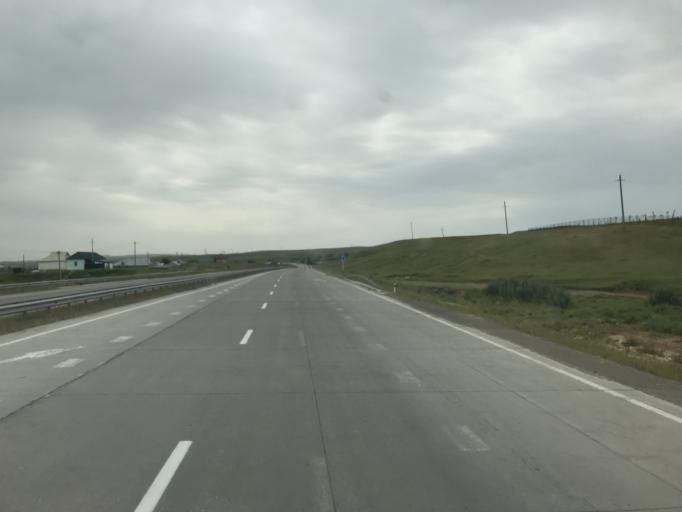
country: KZ
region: Ongtustik Qazaqstan
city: Qazyqurt
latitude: 41.8735
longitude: 69.4263
